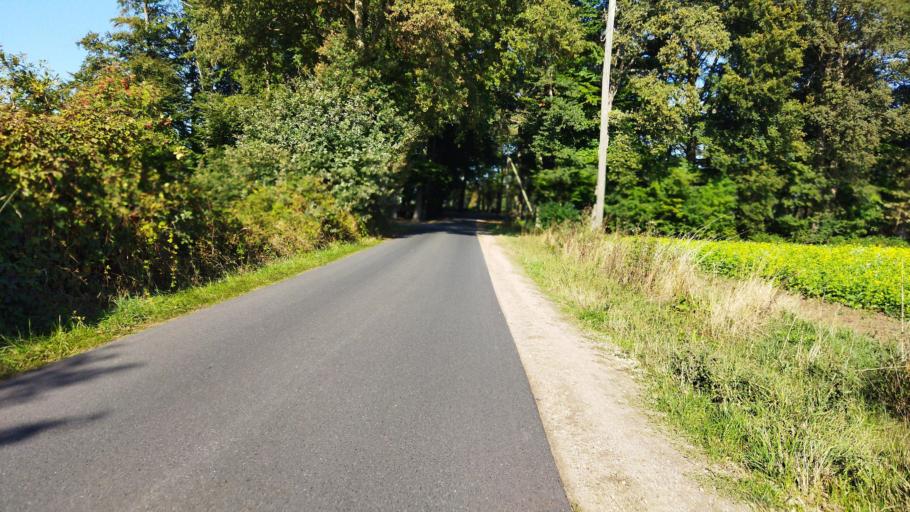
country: DE
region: North Rhine-Westphalia
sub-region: Regierungsbezirk Munster
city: Wettringen
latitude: 52.2335
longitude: 7.3139
